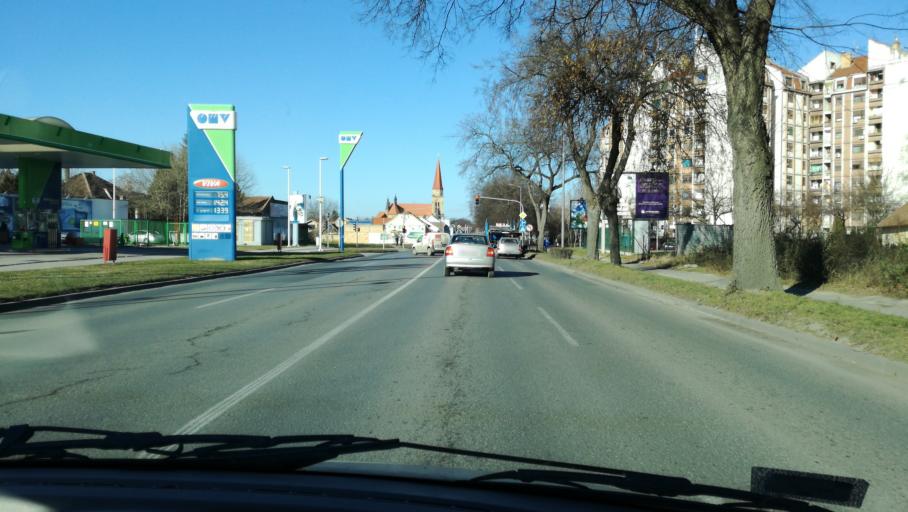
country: RS
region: Autonomna Pokrajina Vojvodina
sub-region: Severnobacki Okrug
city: Subotica
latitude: 46.0858
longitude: 19.6704
